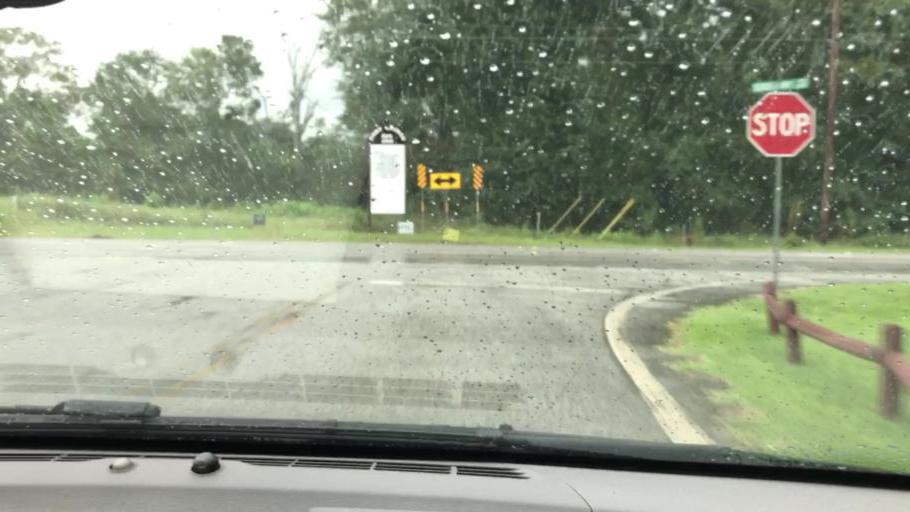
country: US
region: Georgia
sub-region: Clay County
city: Fort Gaines
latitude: 31.6633
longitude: -85.0502
